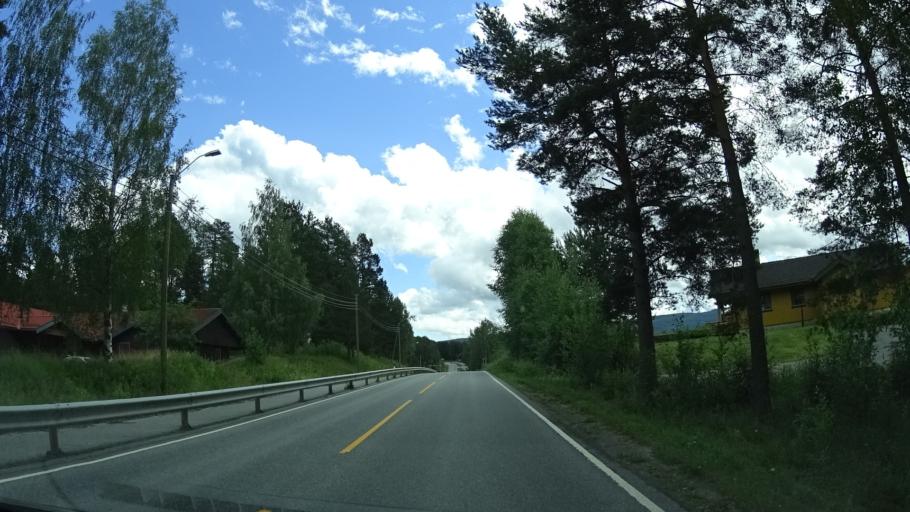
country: NO
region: Buskerud
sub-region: Krodsherad
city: Noresund
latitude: 60.1838
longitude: 9.6160
